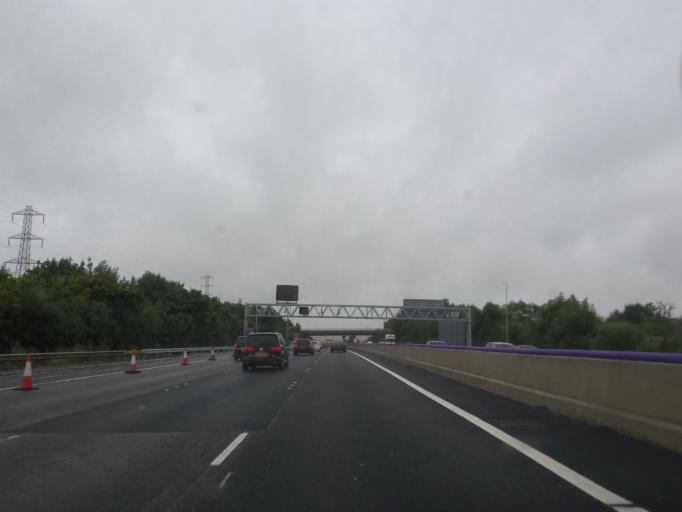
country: GB
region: England
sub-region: Derbyshire
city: Staveley
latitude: 53.2391
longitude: -1.3326
